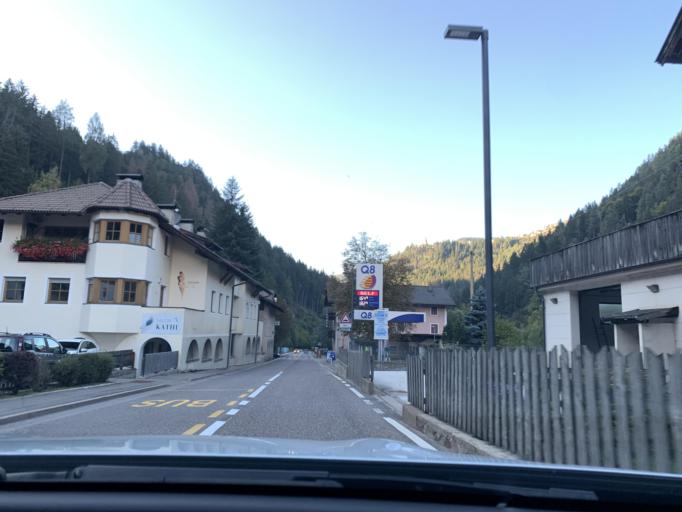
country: IT
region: Trentino-Alto Adige
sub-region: Bolzano
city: Nova Ponente
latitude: 46.4257
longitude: 11.4803
